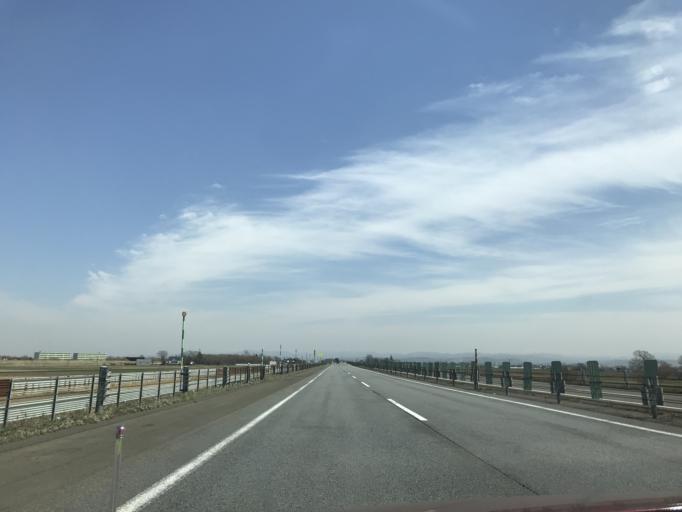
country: JP
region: Hokkaido
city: Iwamizawa
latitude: 43.1368
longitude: 141.6628
